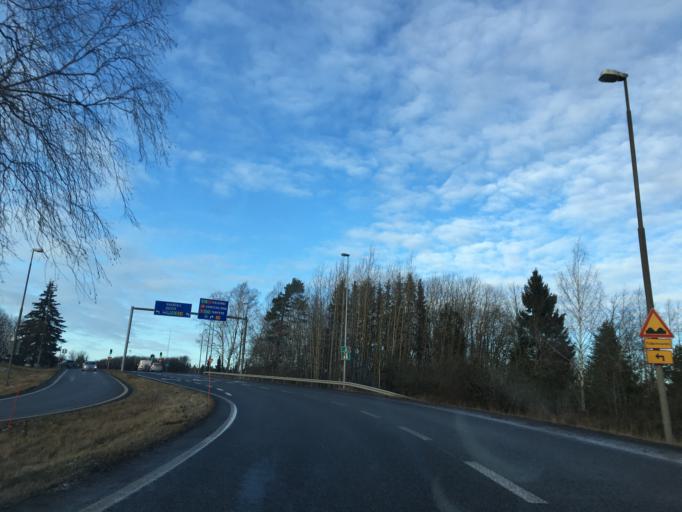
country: FI
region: Varsinais-Suomi
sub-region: Turku
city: Raisio
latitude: 60.4873
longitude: 22.1773
